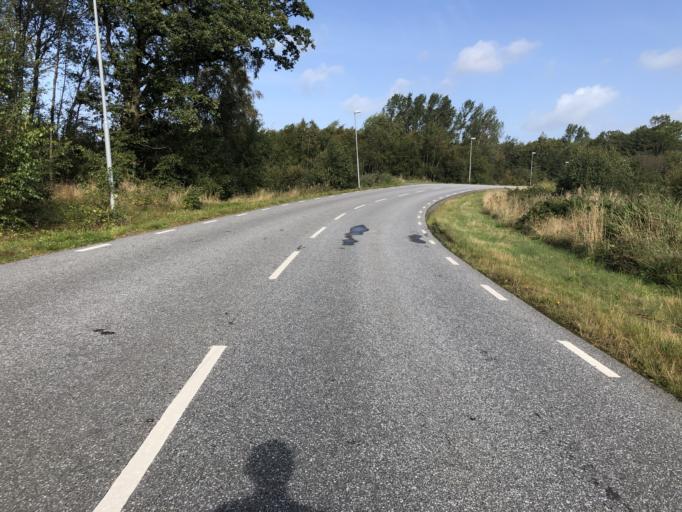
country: SE
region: Vaestra Goetaland
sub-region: Goteborg
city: Torslanda
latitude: 57.7319
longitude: 11.8442
